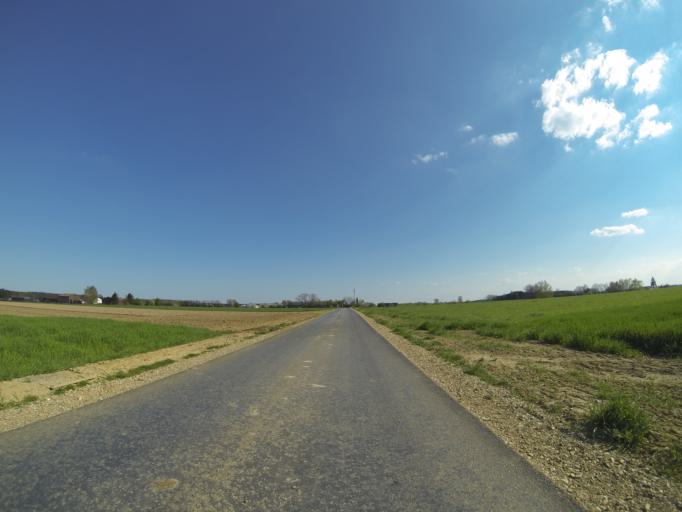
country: DE
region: Baden-Wuerttemberg
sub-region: Tuebingen Region
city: Burgrieden
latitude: 48.2443
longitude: 9.9430
